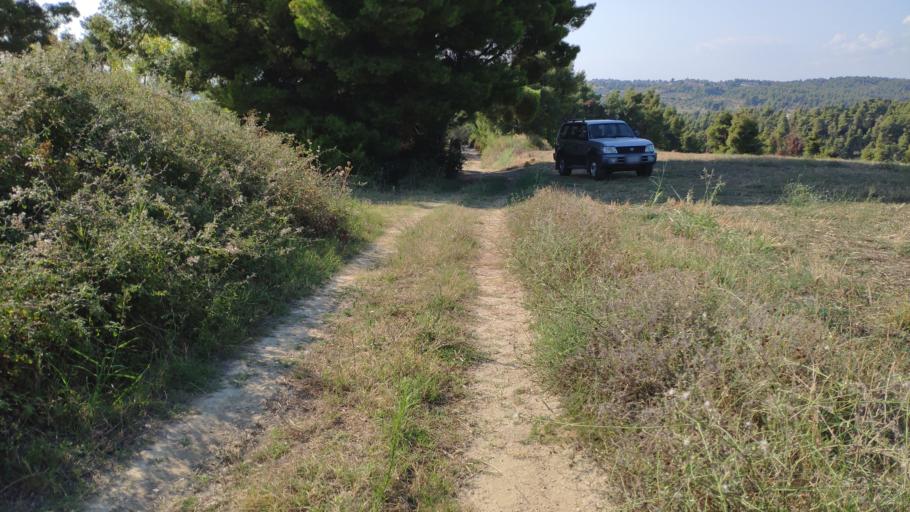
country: GR
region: Central Macedonia
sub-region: Nomos Chalkidikis
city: Kassandreia
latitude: 40.0299
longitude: 23.3678
